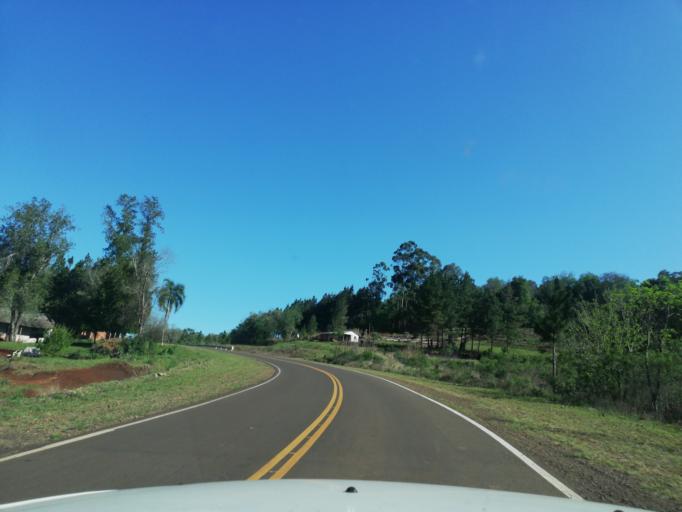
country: AR
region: Misiones
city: Arroyo del Medio
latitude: -27.6768
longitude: -55.4002
